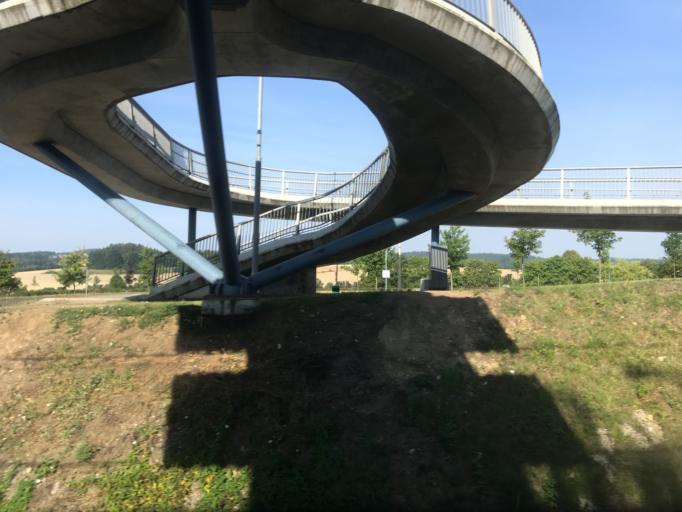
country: CZ
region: Jihocesky
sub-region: Okres Tabor
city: Sezimovo Usti
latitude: 49.4033
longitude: 14.6828
